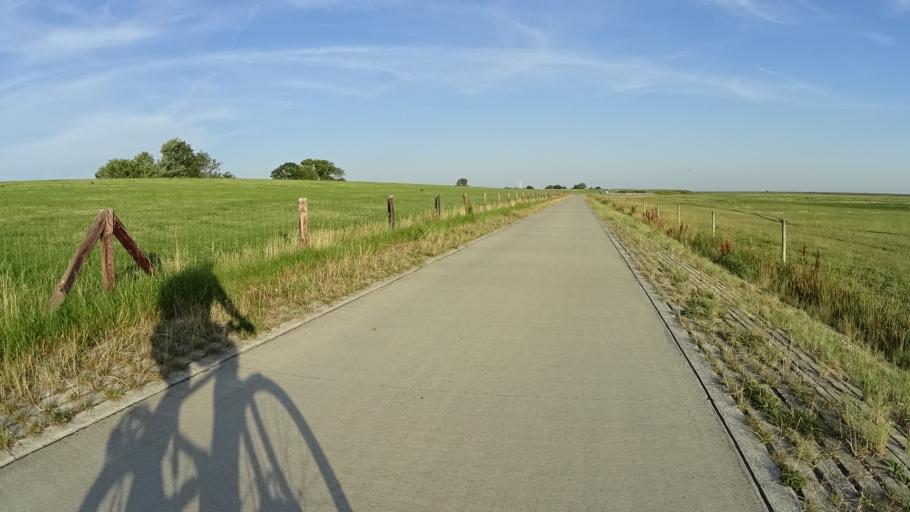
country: DE
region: Lower Saxony
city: Butjadingen
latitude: 53.6064
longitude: 8.3307
